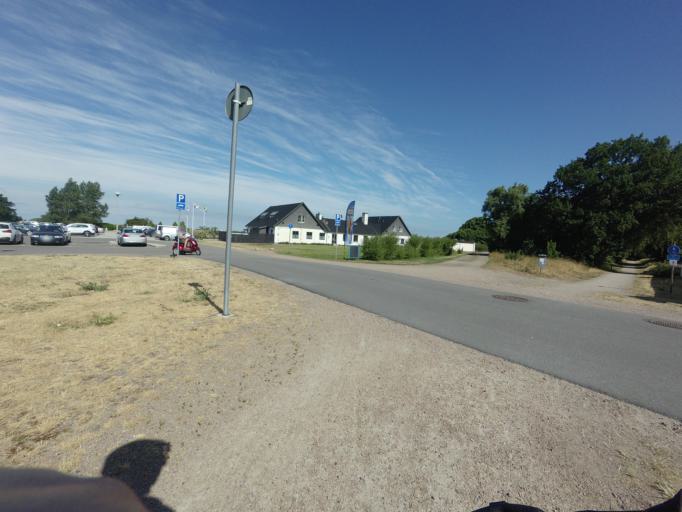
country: SE
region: Skane
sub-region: Vellinge Kommun
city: Skanor med Falsterbo
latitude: 55.3931
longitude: 12.8285
